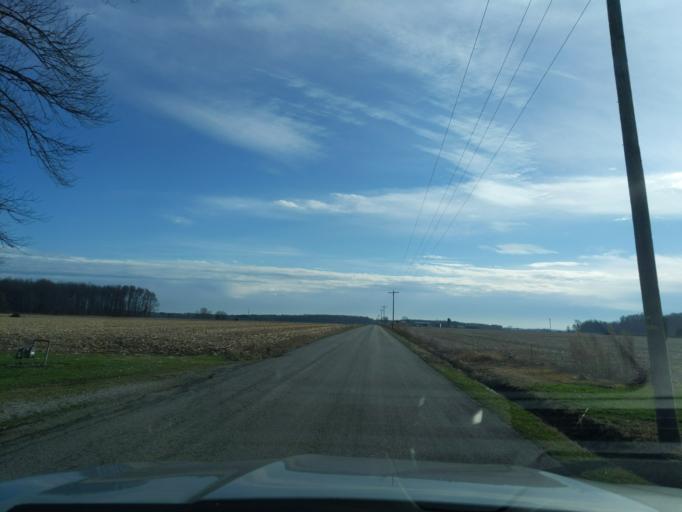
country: US
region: Indiana
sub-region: Decatur County
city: Westport
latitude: 39.2084
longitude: -85.4636
